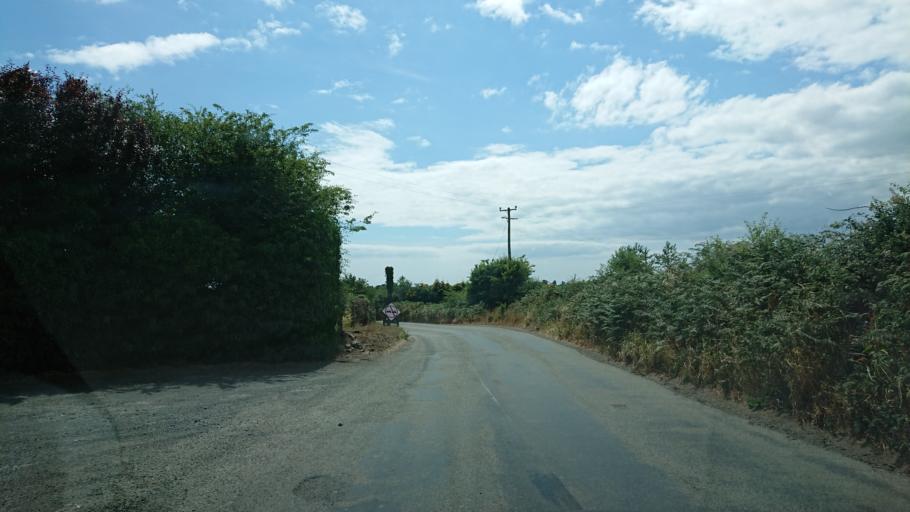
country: IE
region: Munster
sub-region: Waterford
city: Portlaw
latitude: 52.1892
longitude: -7.3324
